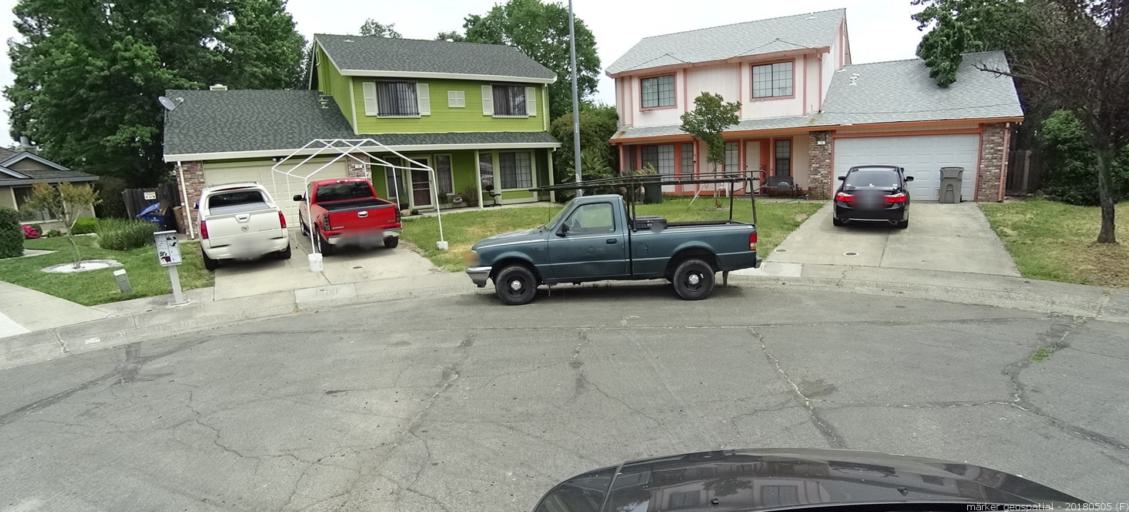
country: US
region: California
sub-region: Sacramento County
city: Rio Linda
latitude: 38.6521
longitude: -121.4619
